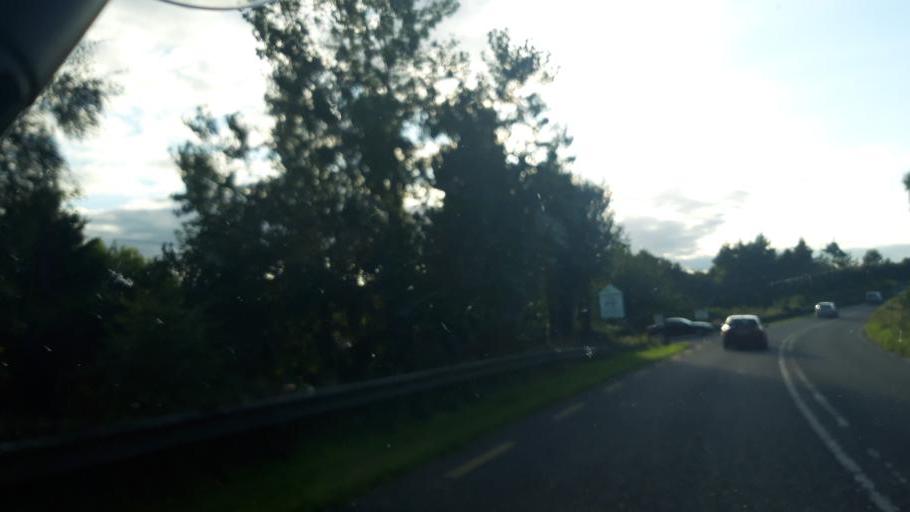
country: IE
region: Leinster
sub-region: Lu
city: Carlingford
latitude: 53.9942
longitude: -6.2216
